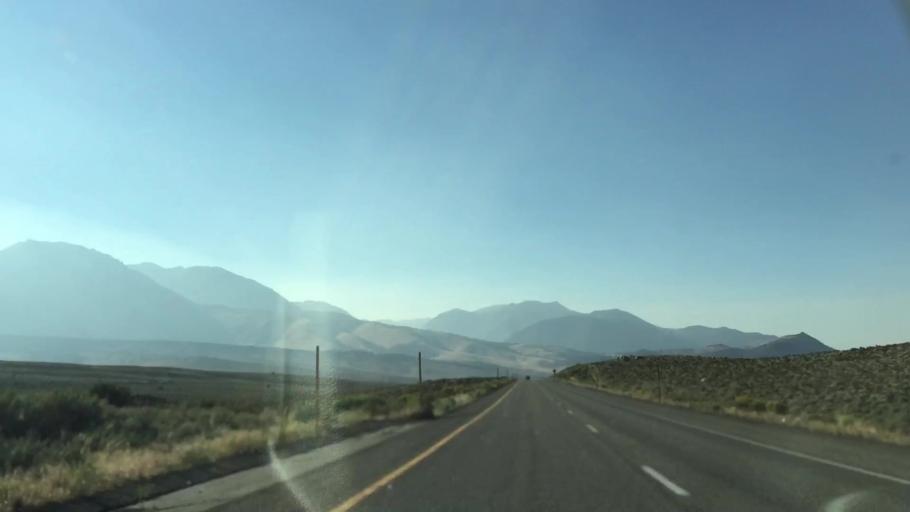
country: US
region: California
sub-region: Mono County
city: Mammoth Lakes
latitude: 37.8449
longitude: -119.0745
